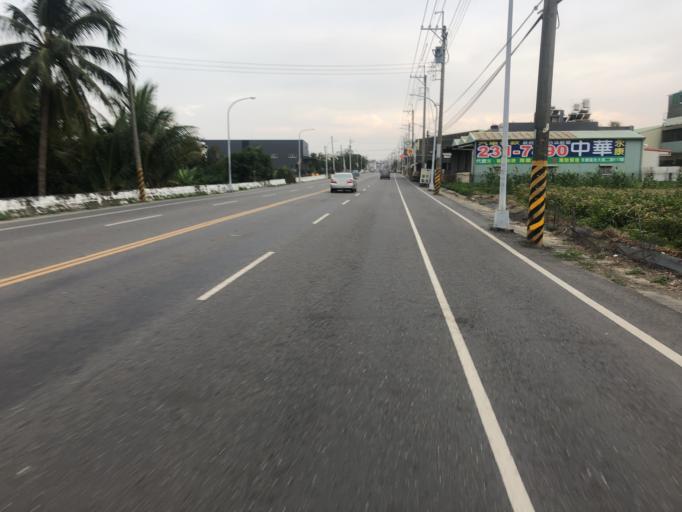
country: TW
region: Taiwan
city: Xinying
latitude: 23.1453
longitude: 120.2880
